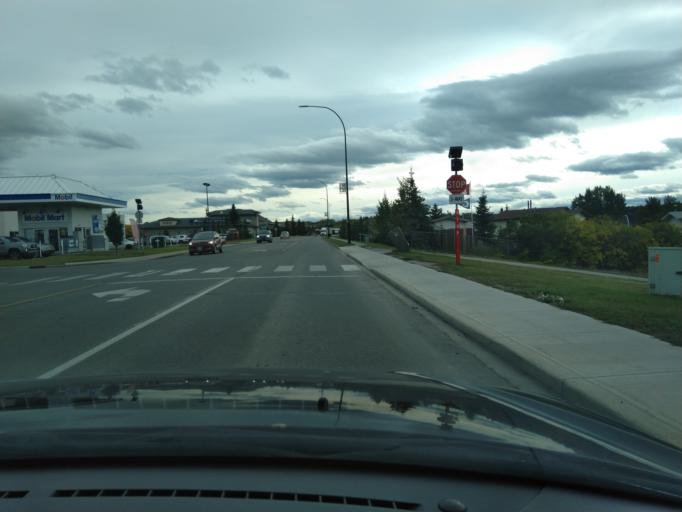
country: CA
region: Alberta
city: Cochrane
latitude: 51.1882
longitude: -114.4757
